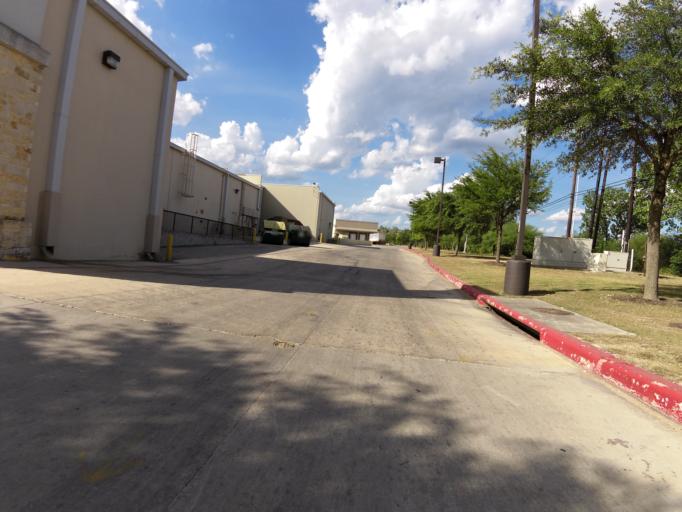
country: US
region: Texas
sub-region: Bexar County
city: Shavano Park
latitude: 29.6068
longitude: -98.5950
